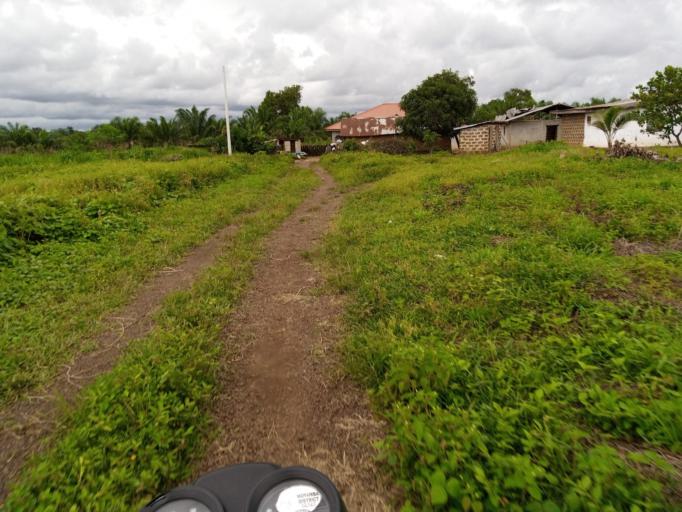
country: SL
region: Southern Province
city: Moyamba
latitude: 8.1696
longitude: -12.4250
